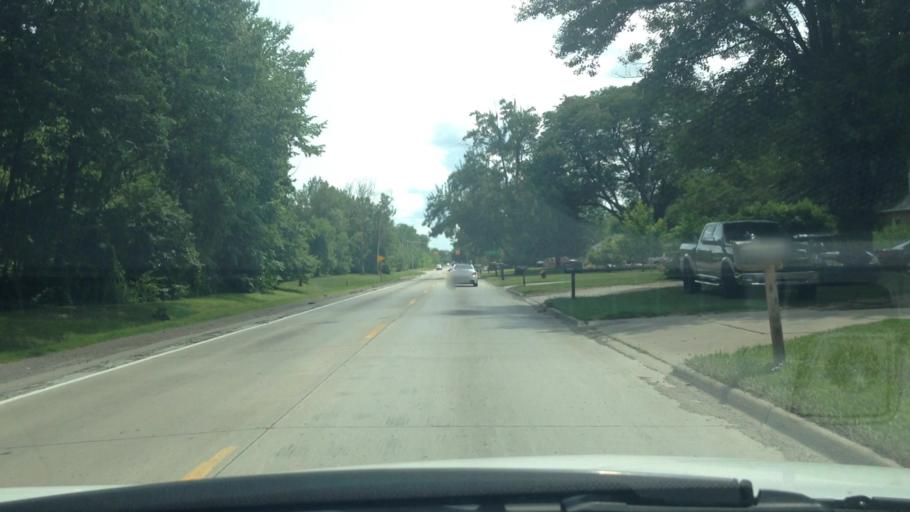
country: US
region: Michigan
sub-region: Wayne County
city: Taylor
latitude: 42.2278
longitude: -83.3077
